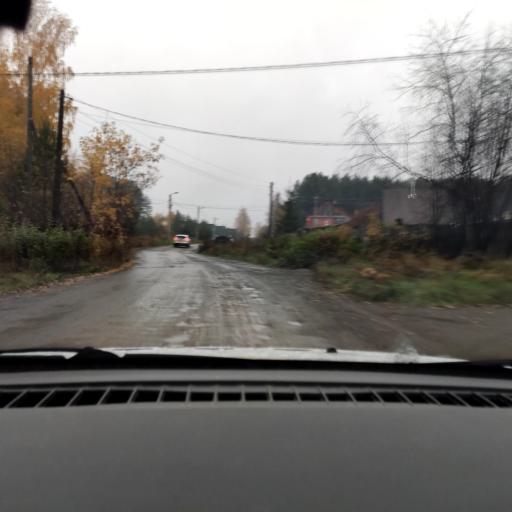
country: RU
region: Perm
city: Kondratovo
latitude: 58.0479
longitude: 56.1036
